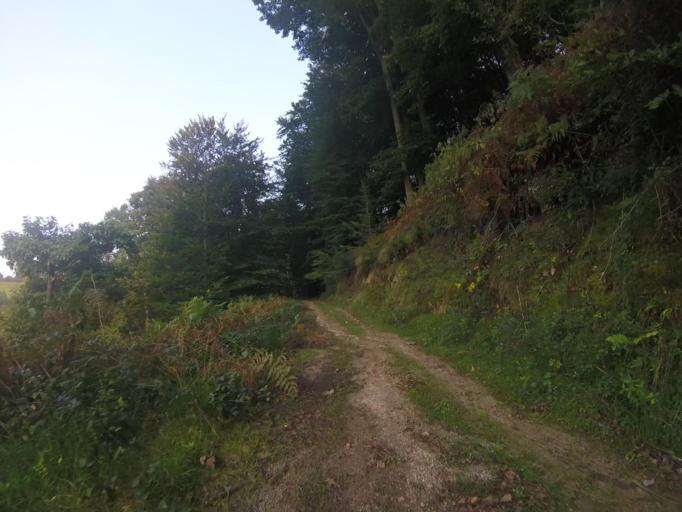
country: ES
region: Basque Country
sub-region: Provincia de Guipuzcoa
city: Errenteria
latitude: 43.2600
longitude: -1.8338
